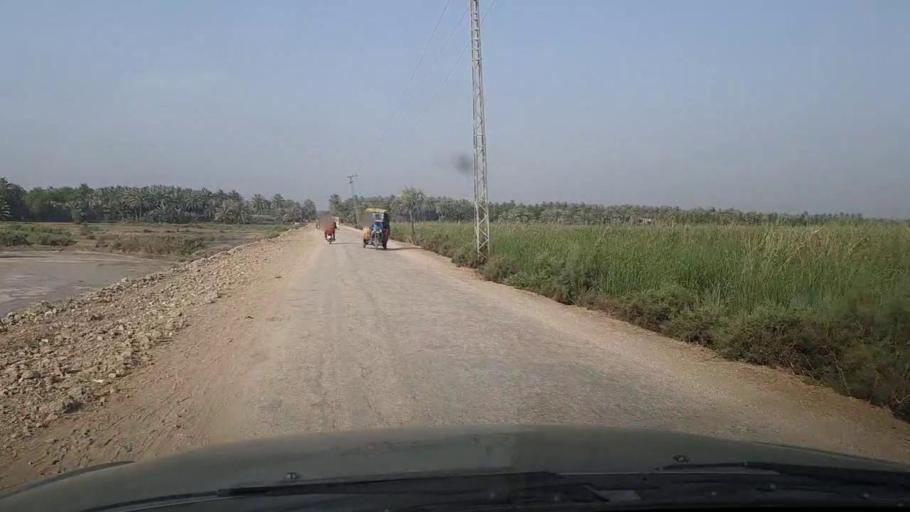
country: PK
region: Sindh
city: Pir jo Goth
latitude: 27.5626
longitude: 68.5698
